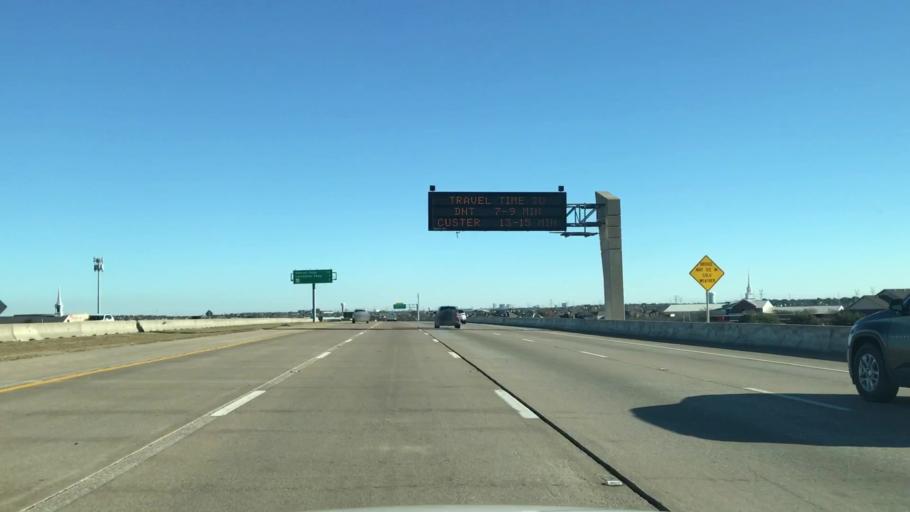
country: US
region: Texas
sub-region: Denton County
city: Lewisville
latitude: 33.0104
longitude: -96.9451
